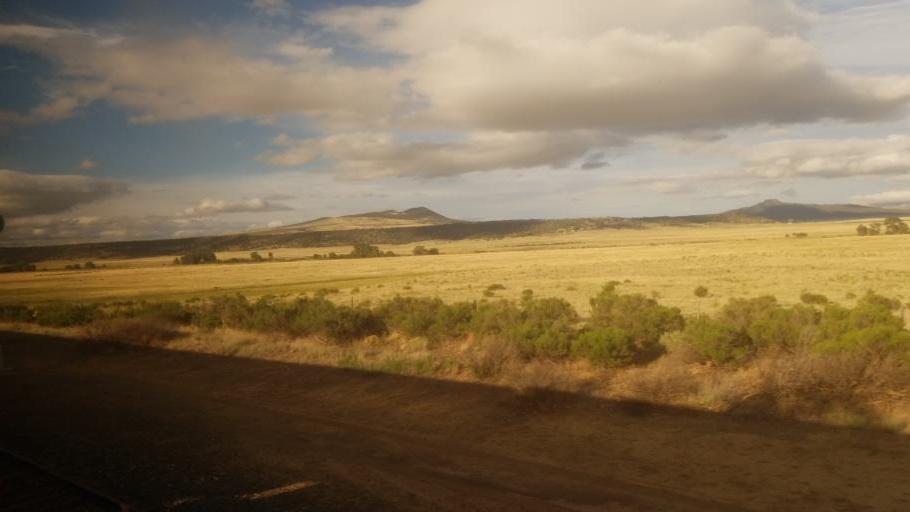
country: US
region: New Mexico
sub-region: Colfax County
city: Raton
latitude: 36.6403
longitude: -104.4990
